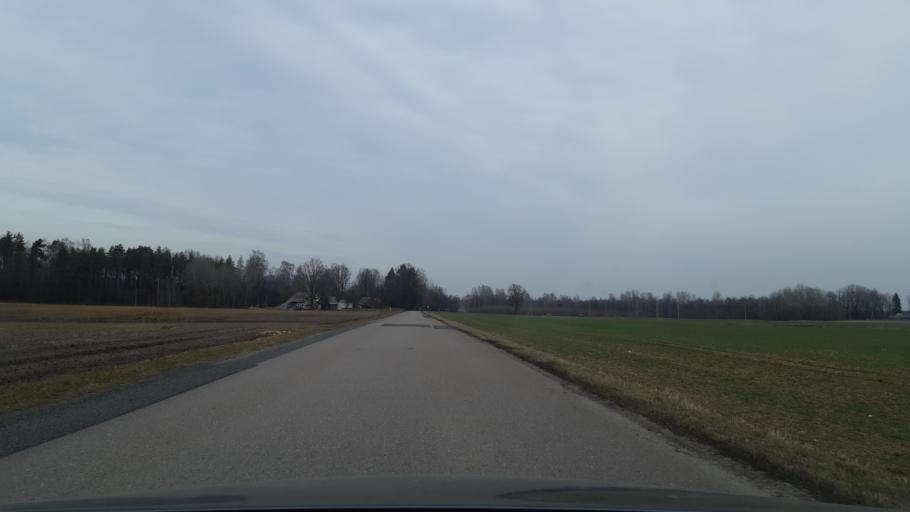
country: LT
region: Marijampoles apskritis
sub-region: Marijampole Municipality
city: Marijampole
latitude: 54.7295
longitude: 23.3379
